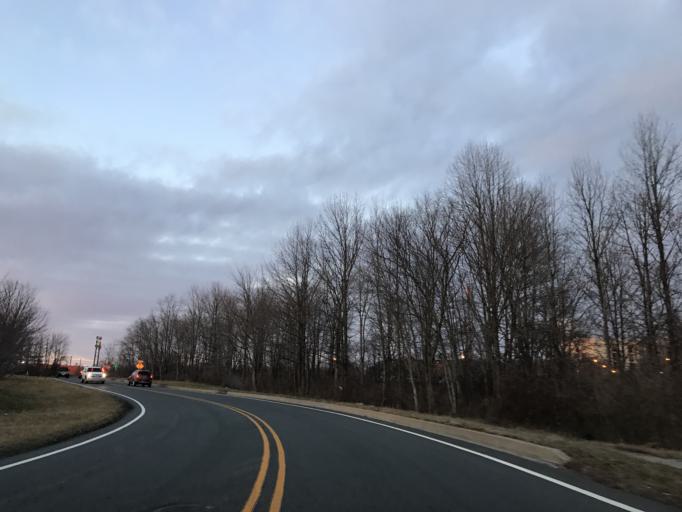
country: US
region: Maryland
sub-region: Cecil County
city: Elkton
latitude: 39.6356
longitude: -75.8050
